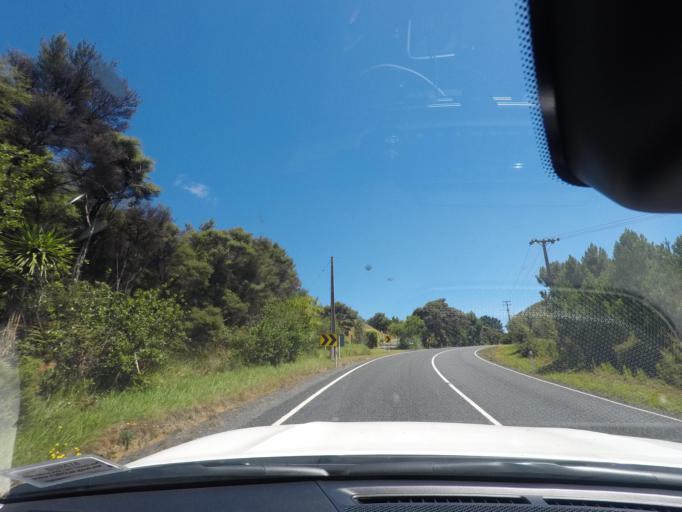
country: NZ
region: Auckland
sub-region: Auckland
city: Parakai
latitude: -36.5837
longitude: 174.3305
